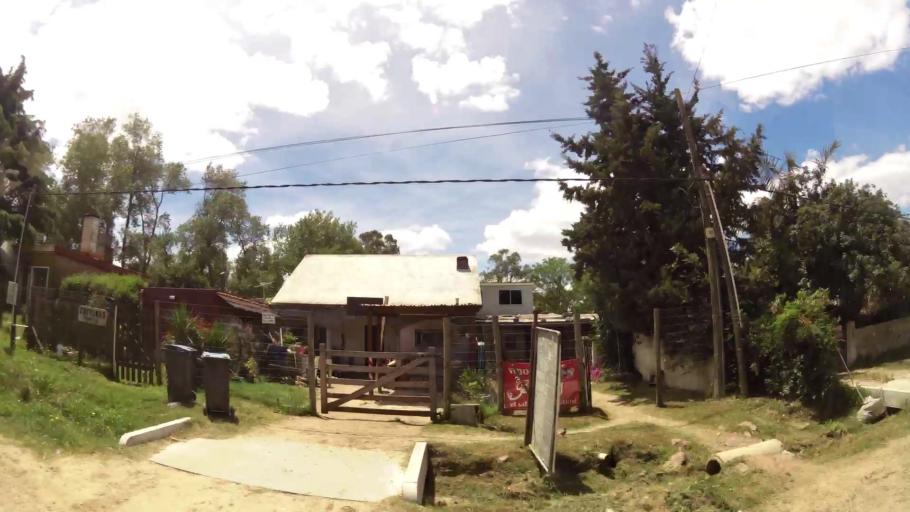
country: UY
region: Canelones
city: Colonia Nicolich
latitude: -34.8210
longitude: -55.9701
